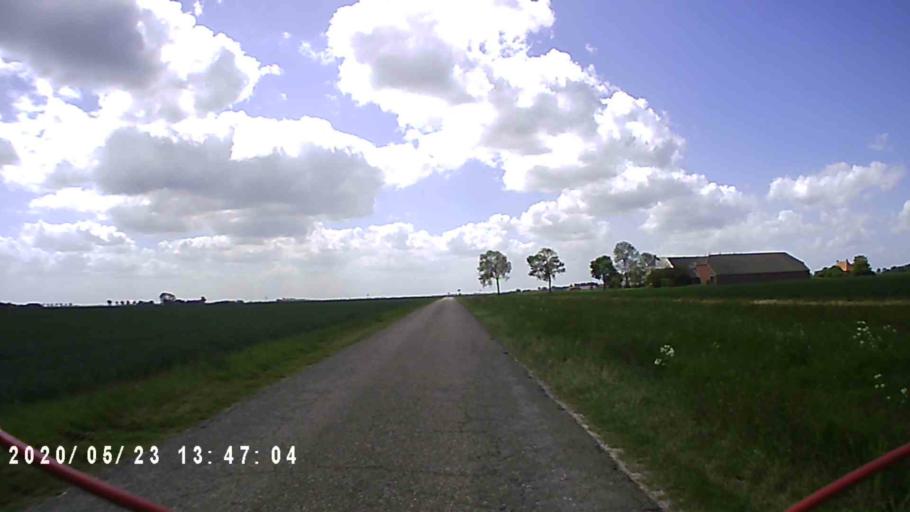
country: NL
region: Groningen
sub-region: Gemeente  Oldambt
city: Winschoten
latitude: 53.2627
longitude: 7.0581
